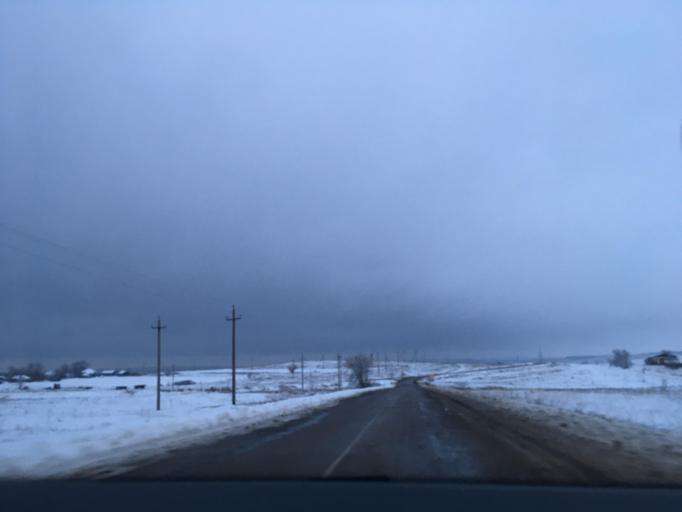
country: RU
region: Voronezj
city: Verkhniy Mamon
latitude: 50.0723
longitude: 40.3031
